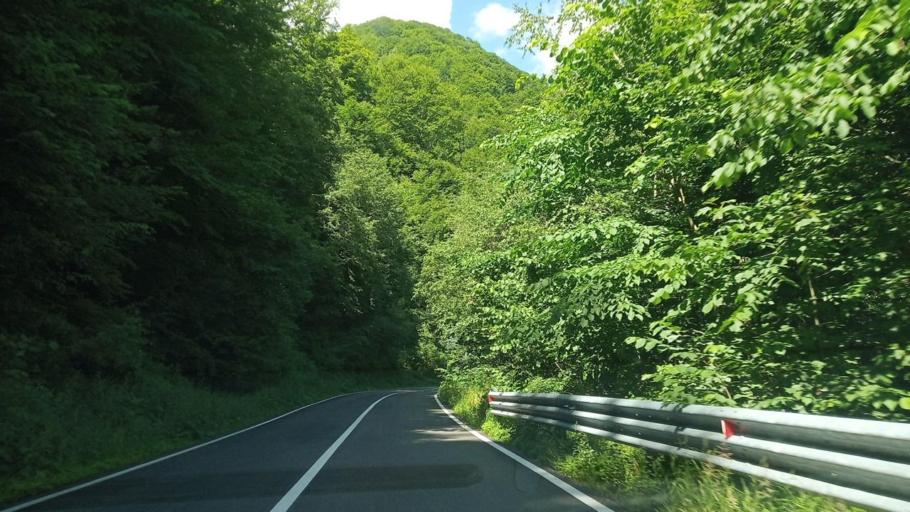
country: RO
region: Alba
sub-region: Comuna Sugag
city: Sugag
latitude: 45.6929
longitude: 23.6012
